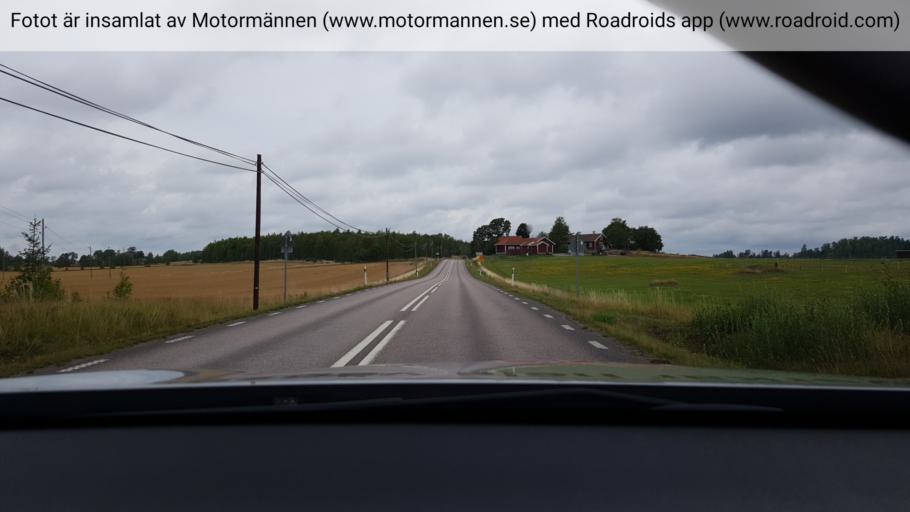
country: SE
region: Soedermanland
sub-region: Gnesta Kommun
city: Gnesta
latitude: 59.0532
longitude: 17.2502
